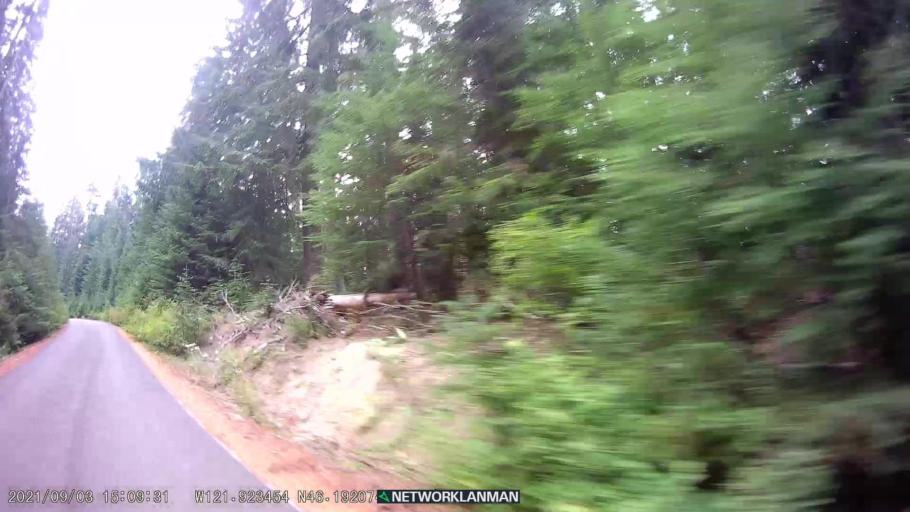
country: US
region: Washington
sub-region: Skamania County
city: Carson
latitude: 46.1920
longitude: -121.9236
